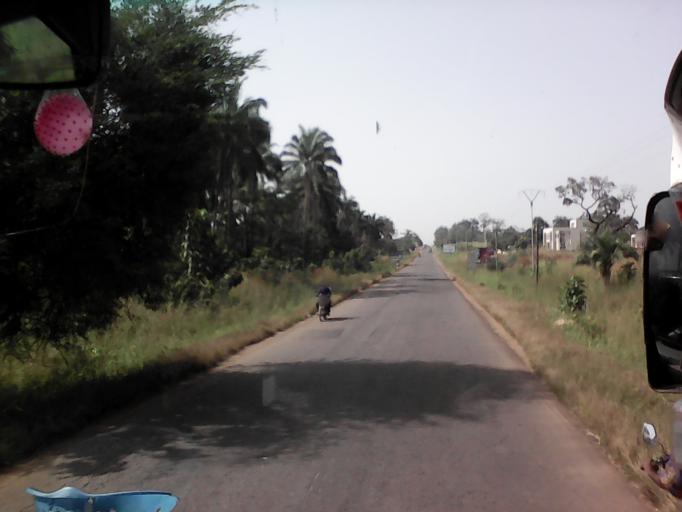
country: TG
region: Centrale
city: Sokode
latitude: 8.9592
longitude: 1.1363
